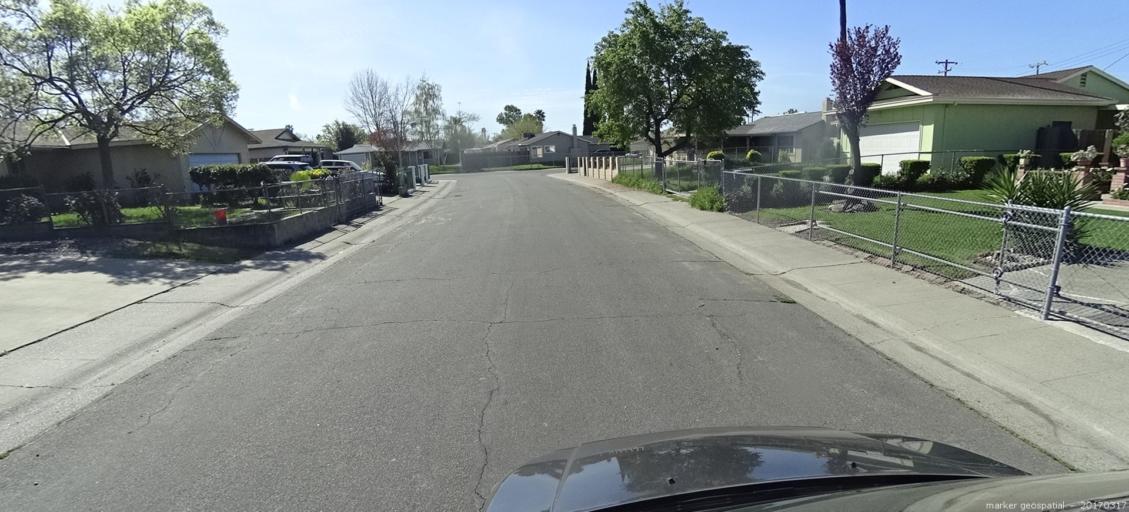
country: US
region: California
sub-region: Sacramento County
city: Parkway
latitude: 38.4869
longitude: -121.4886
